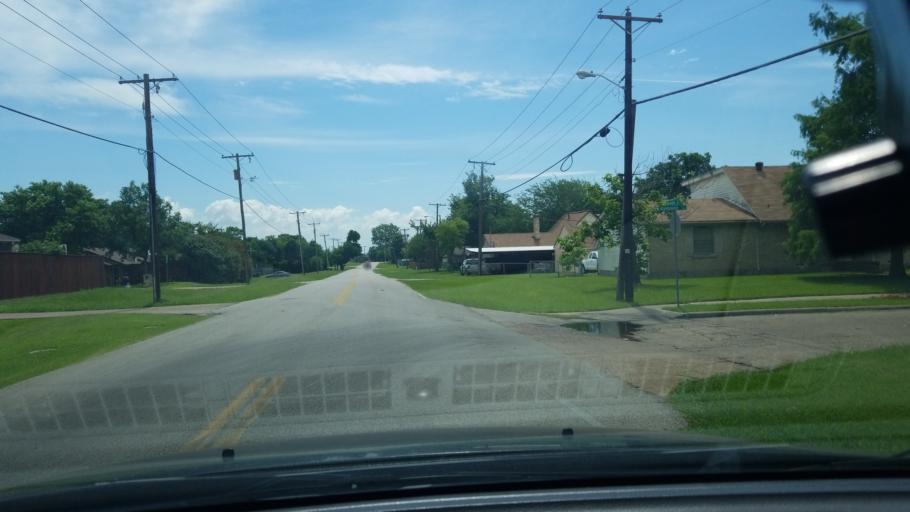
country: US
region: Texas
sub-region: Dallas County
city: Mesquite
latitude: 32.7605
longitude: -96.5813
